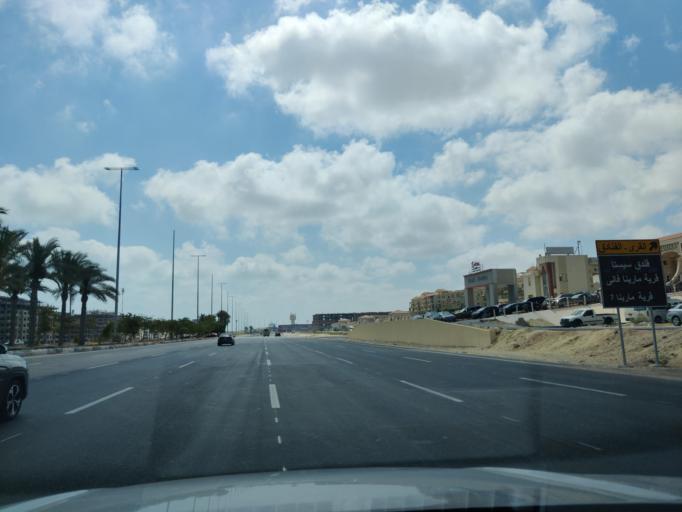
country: EG
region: Muhafazat Matruh
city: Al `Alamayn
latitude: 30.8457
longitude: 28.9333
